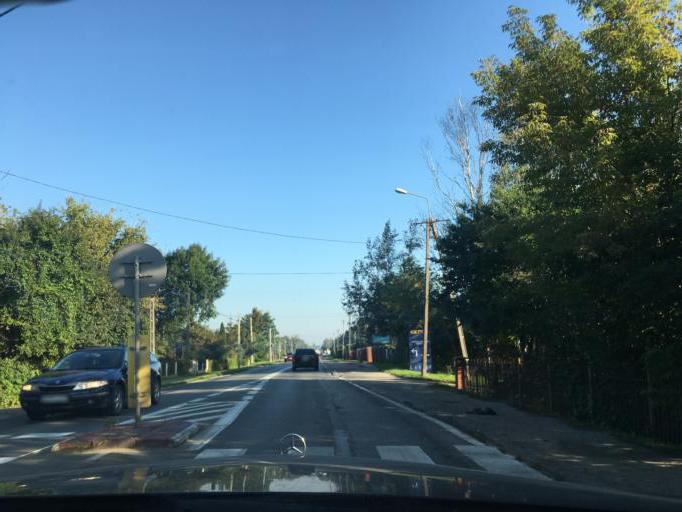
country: PL
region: Masovian Voivodeship
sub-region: Powiat grodziski
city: Grodzisk Mazowiecki
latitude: 52.1310
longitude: 20.6181
